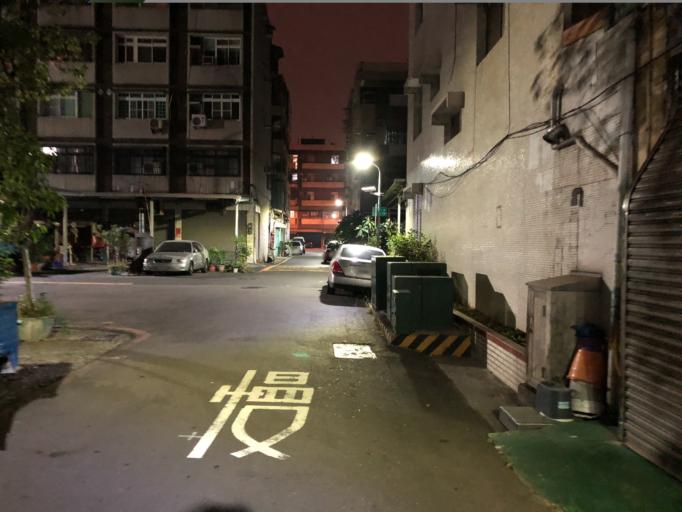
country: TW
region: Kaohsiung
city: Kaohsiung
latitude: 22.6380
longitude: 120.3329
